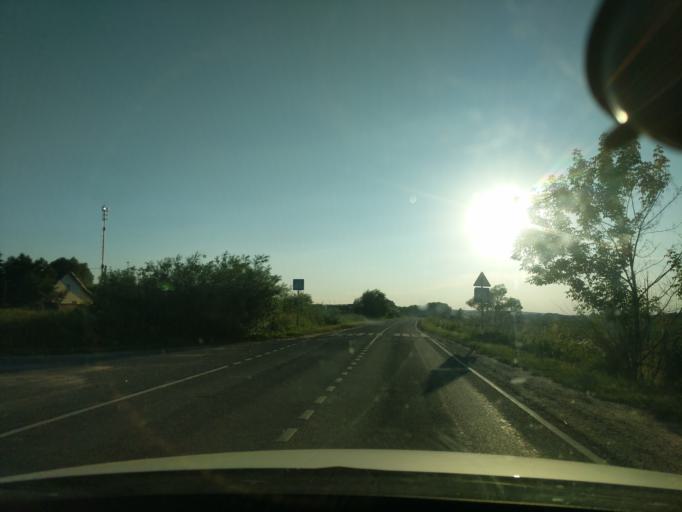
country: RU
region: Moskovskaya
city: Pushchino
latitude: 54.8434
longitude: 37.5383
